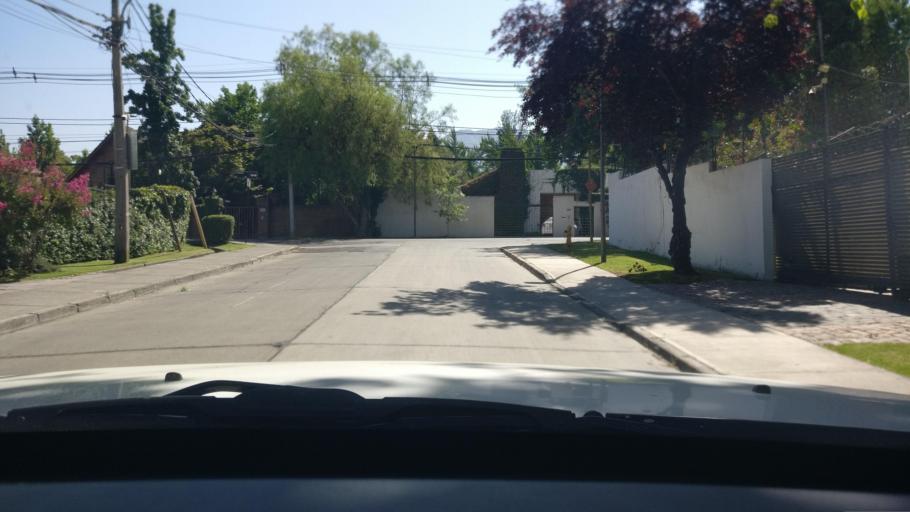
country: CL
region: Santiago Metropolitan
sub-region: Provincia de Santiago
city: Villa Presidente Frei, Nunoa, Santiago, Chile
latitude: -33.3745
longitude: -70.5114
